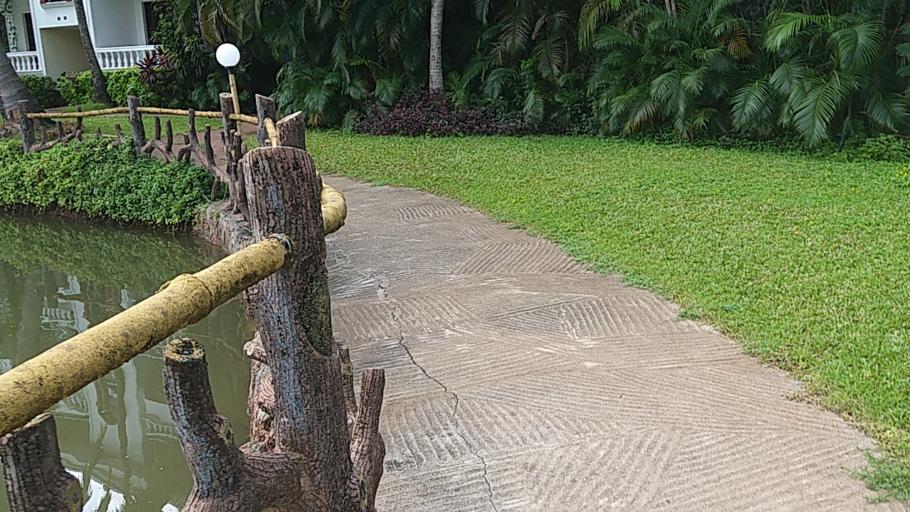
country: IN
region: Goa
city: Calangute
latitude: 15.5661
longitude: 73.7587
